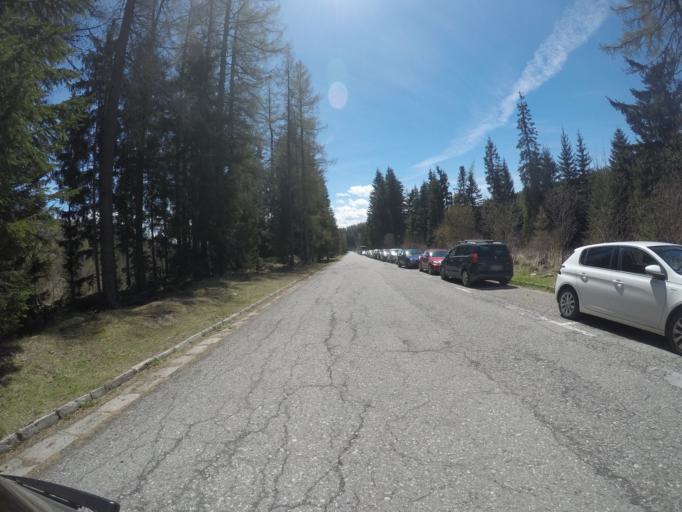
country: SK
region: Presovsky
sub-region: Okres Poprad
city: Strba
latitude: 49.1248
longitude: 20.0747
